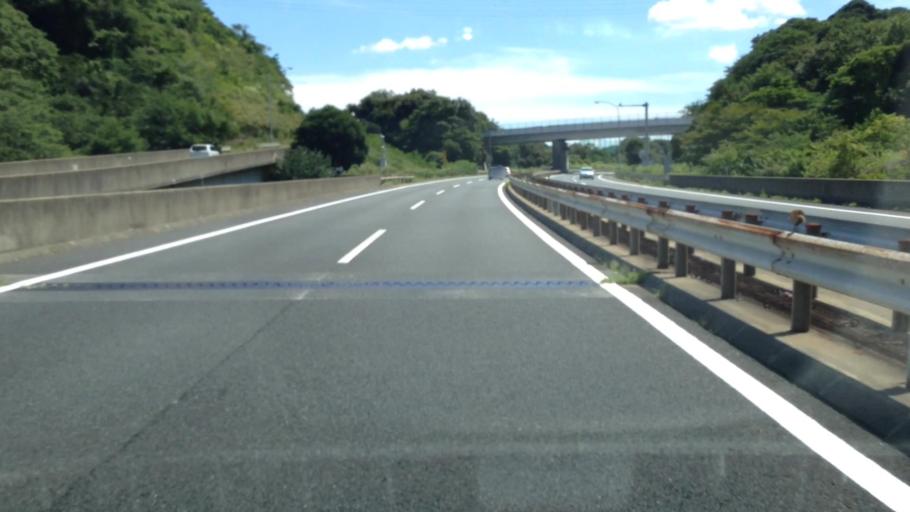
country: JP
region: Kanagawa
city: Yokosuka
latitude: 35.2785
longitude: 139.6329
